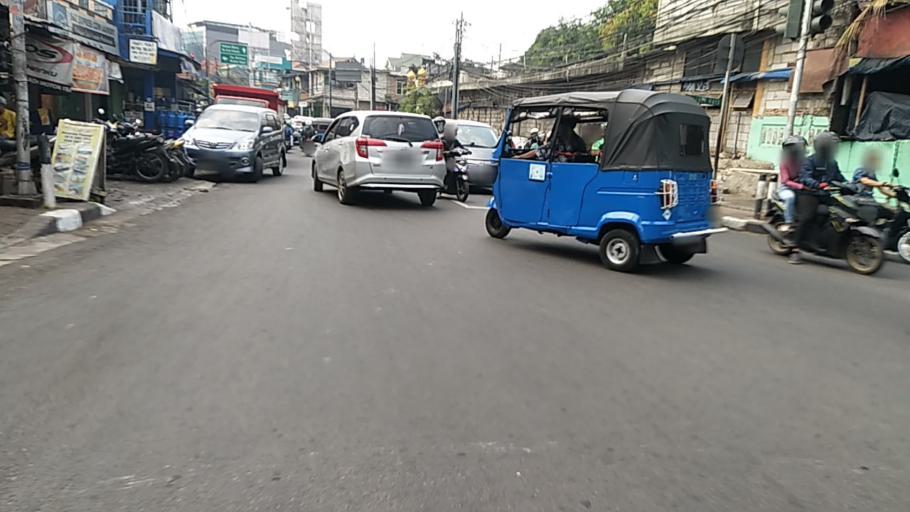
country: ID
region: Jakarta Raya
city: Jakarta
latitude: -6.2302
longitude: 106.8516
